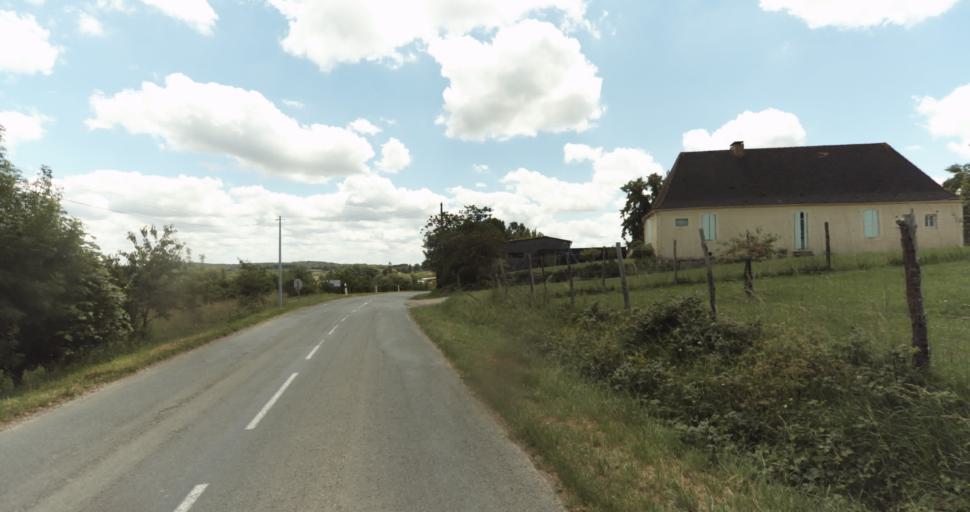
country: FR
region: Aquitaine
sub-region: Departement de la Dordogne
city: Beaumont-du-Perigord
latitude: 44.7264
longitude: 0.7918
